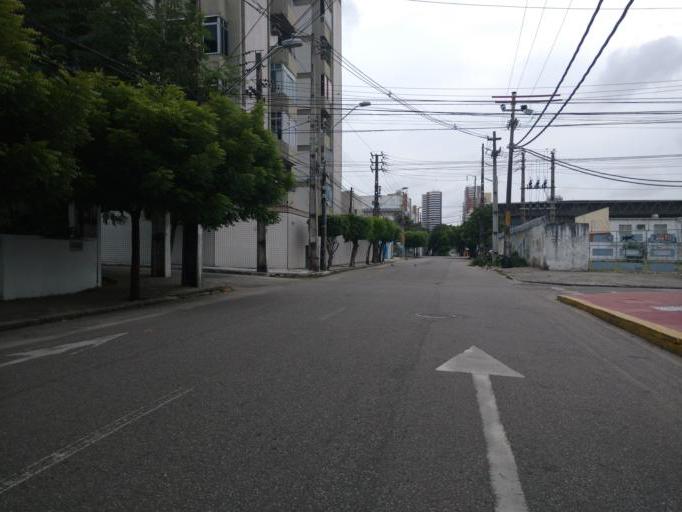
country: BR
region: Ceara
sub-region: Fortaleza
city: Fortaleza
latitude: -3.7370
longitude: -38.5062
